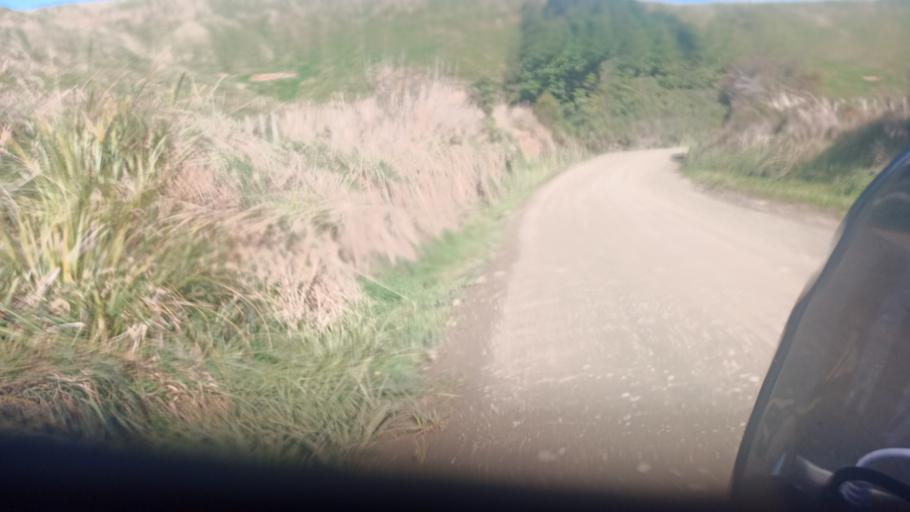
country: NZ
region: Bay of Plenty
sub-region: Opotiki District
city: Opotiki
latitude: -38.4389
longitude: 177.5426
